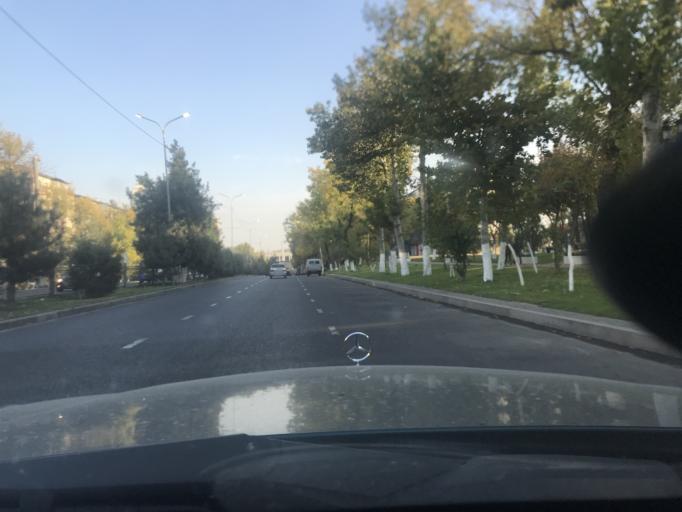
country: KZ
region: Ongtustik Qazaqstan
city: Shymkent
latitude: 42.3028
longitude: 69.6044
